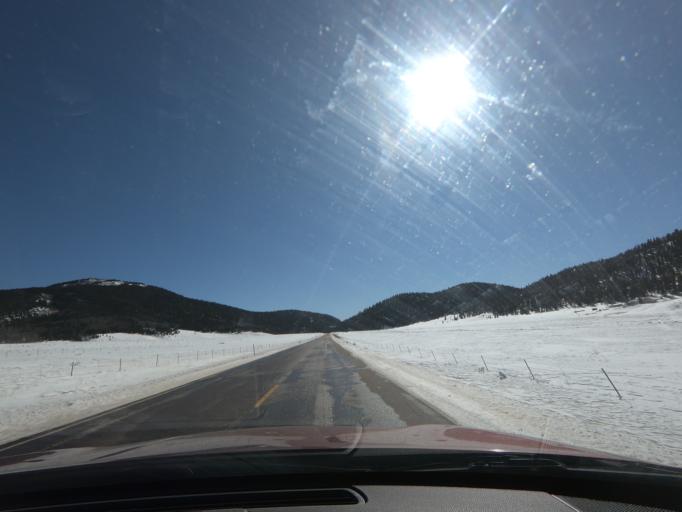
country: US
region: Colorado
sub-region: Teller County
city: Cripple Creek
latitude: 38.7620
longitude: -105.1132
